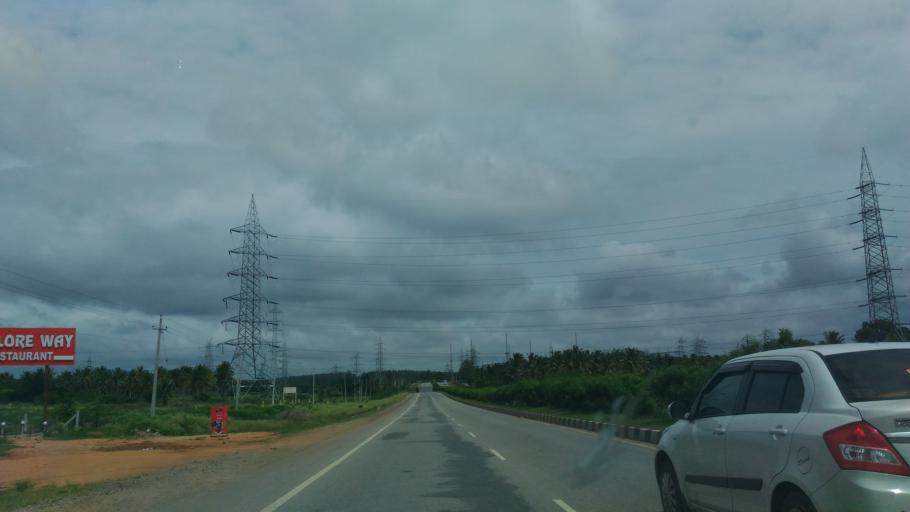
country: IN
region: Karnataka
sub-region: Hassan
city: Hassan
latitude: 12.9874
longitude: 76.2014
